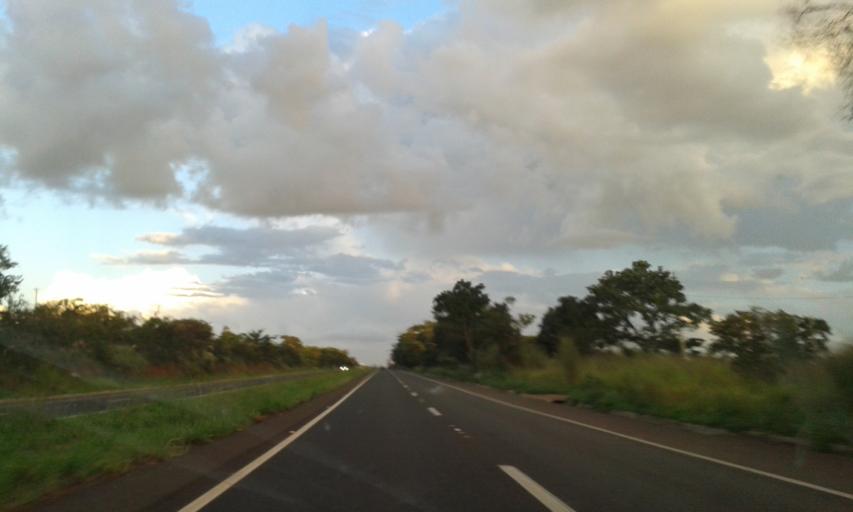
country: BR
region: Minas Gerais
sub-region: Monte Alegre De Minas
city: Monte Alegre de Minas
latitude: -18.8596
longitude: -48.7710
